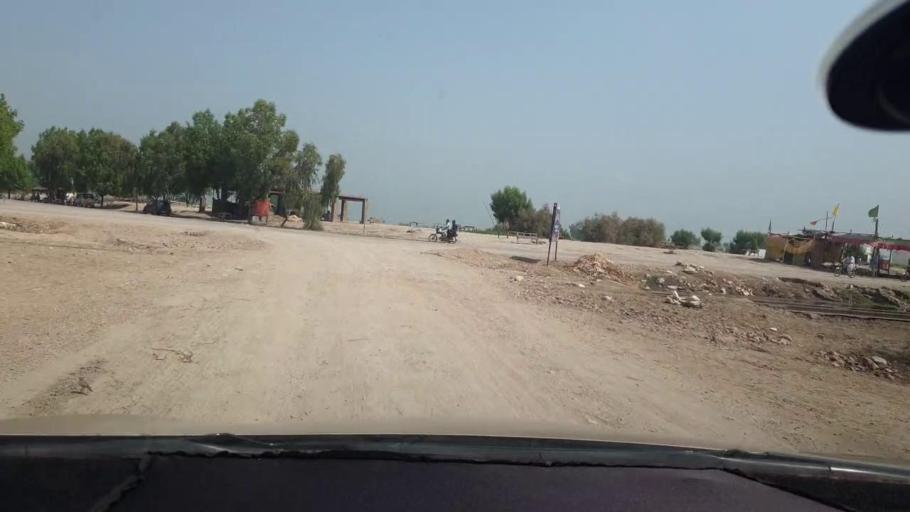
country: PK
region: Sindh
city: Kambar
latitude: 27.5878
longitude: 68.0254
